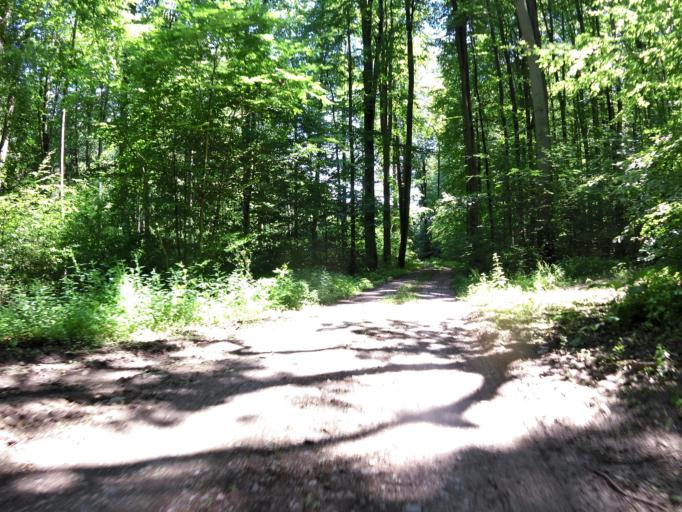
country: DE
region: Bavaria
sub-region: Regierungsbezirk Unterfranken
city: Reichenberg
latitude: 49.7235
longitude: 9.8877
